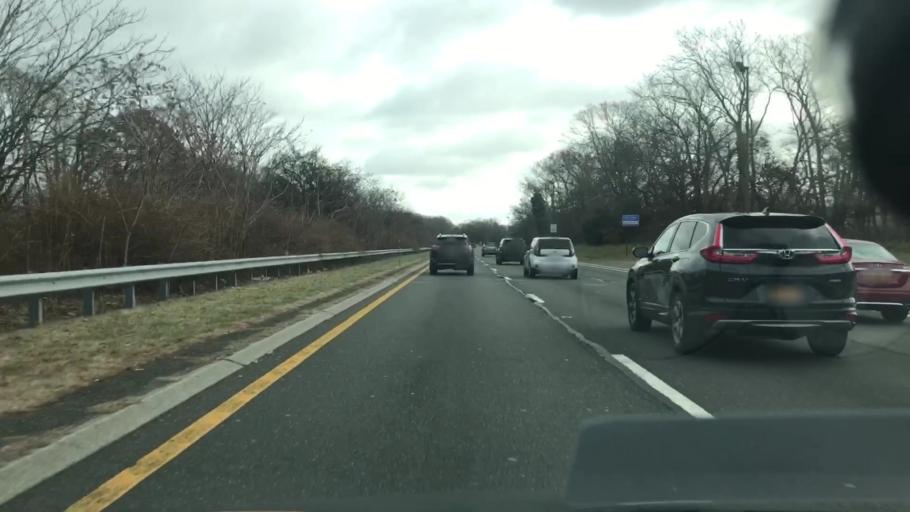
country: US
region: New York
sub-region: Nassau County
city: North Merrick
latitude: 40.6899
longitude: -73.5620
